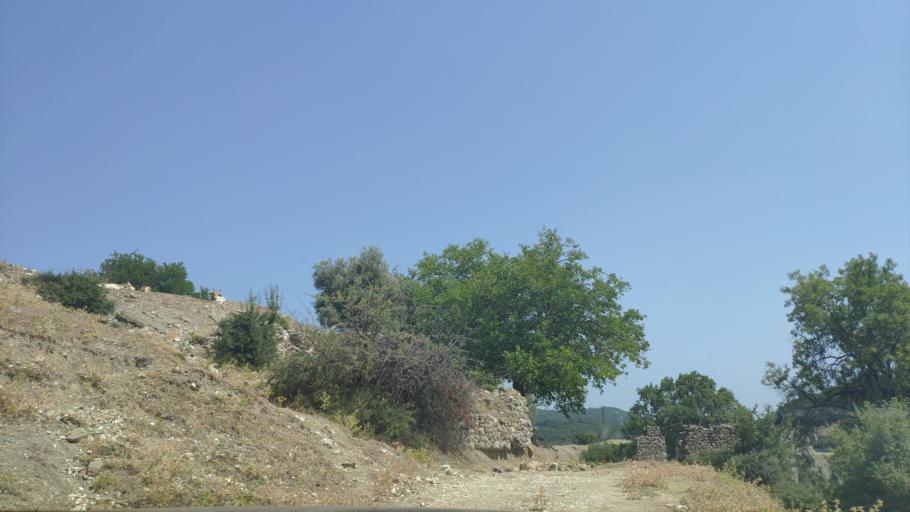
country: GR
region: West Greece
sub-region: Nomos Aitolias kai Akarnanias
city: Monastirakion
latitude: 38.8155
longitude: 21.0173
